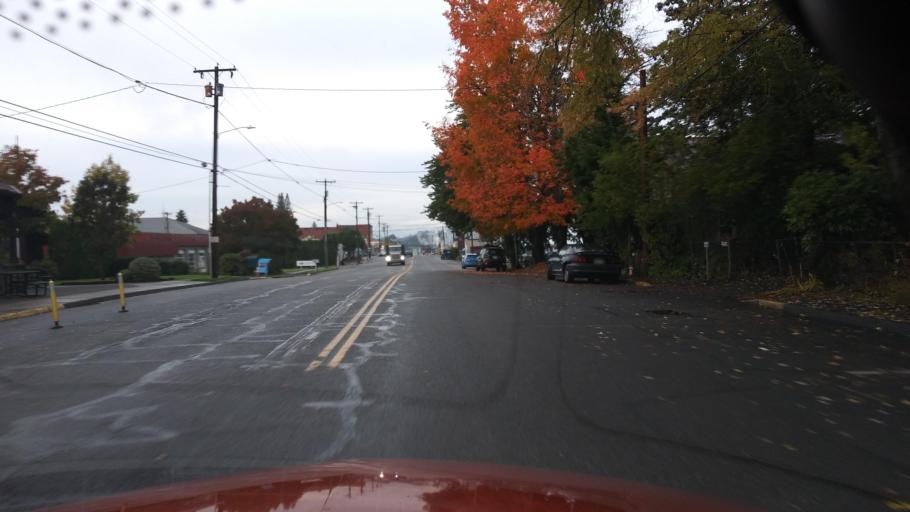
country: US
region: Oregon
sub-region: Washington County
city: North Plains
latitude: 45.5977
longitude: -122.9989
